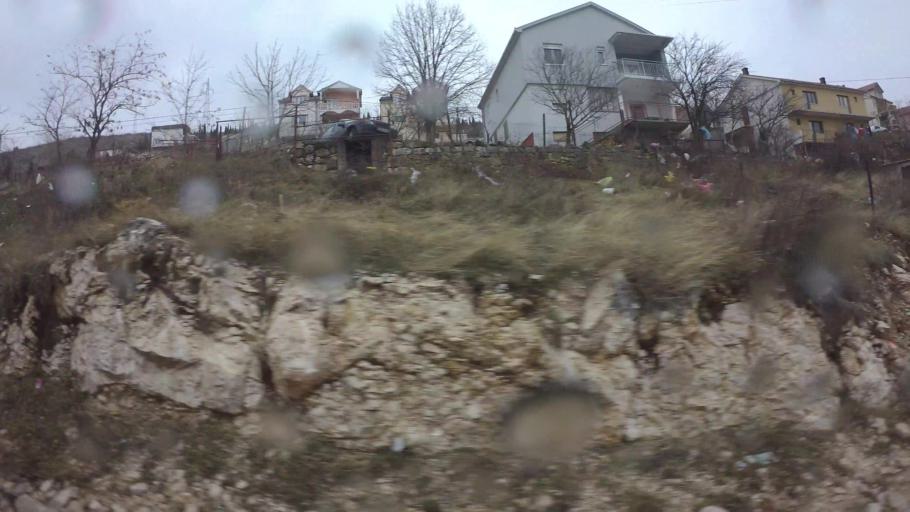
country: BA
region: Federation of Bosnia and Herzegovina
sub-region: Hercegovacko-Bosanski Kanton
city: Mostar
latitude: 43.3540
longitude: 17.8175
